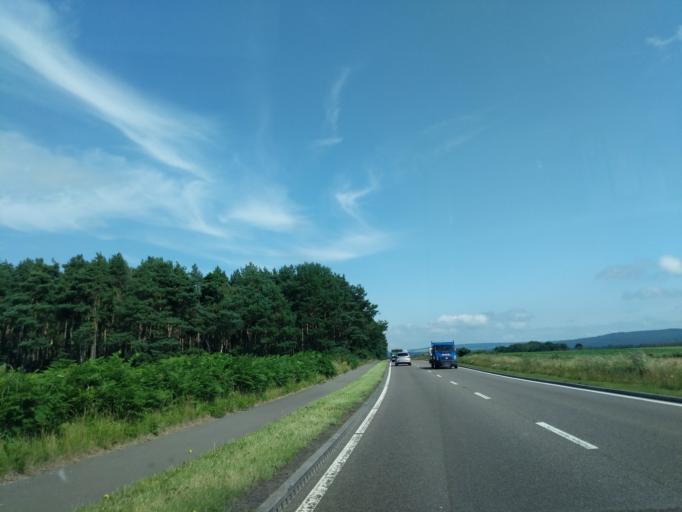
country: GB
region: Scotland
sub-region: Moray
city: Fochabers
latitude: 57.6266
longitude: -3.1535
